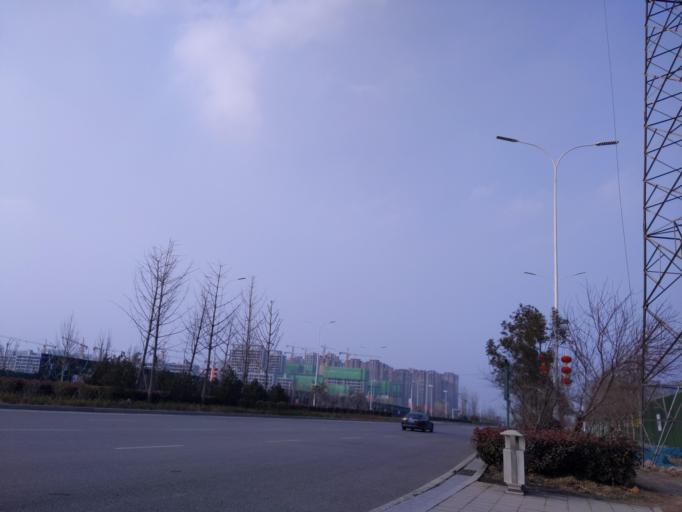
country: CN
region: Henan Sheng
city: Puyang
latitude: 35.8075
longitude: 115.0222
